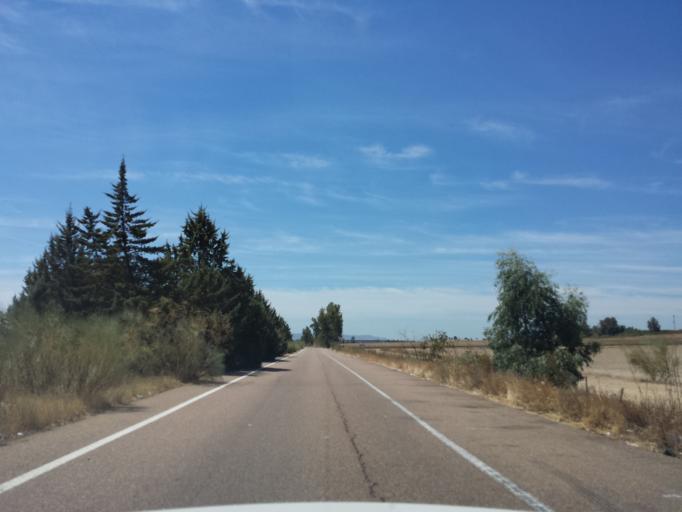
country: ES
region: Extremadura
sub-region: Provincia de Badajoz
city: Santa Amalia
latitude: 39.0052
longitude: -6.0912
